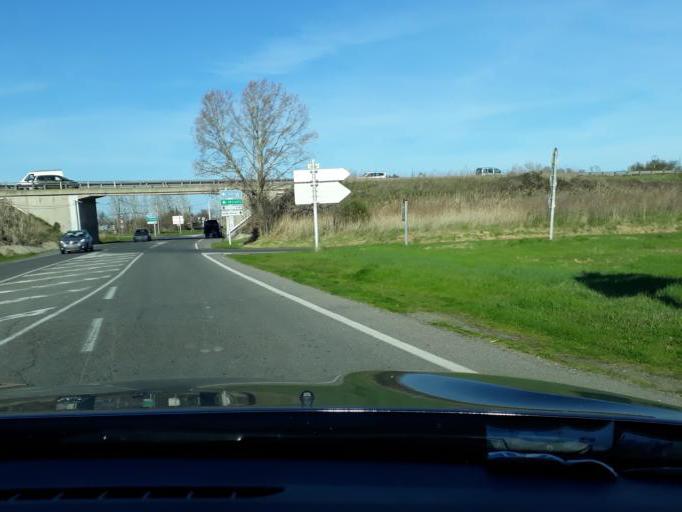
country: FR
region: Languedoc-Roussillon
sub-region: Departement de l'Herault
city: Agde
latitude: 43.3034
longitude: 3.4553
